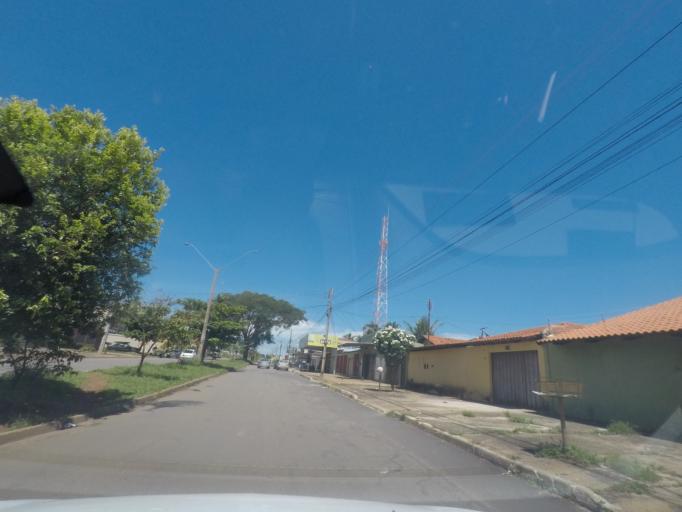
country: BR
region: Goias
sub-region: Aparecida De Goiania
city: Aparecida de Goiania
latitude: -16.7697
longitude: -49.3248
